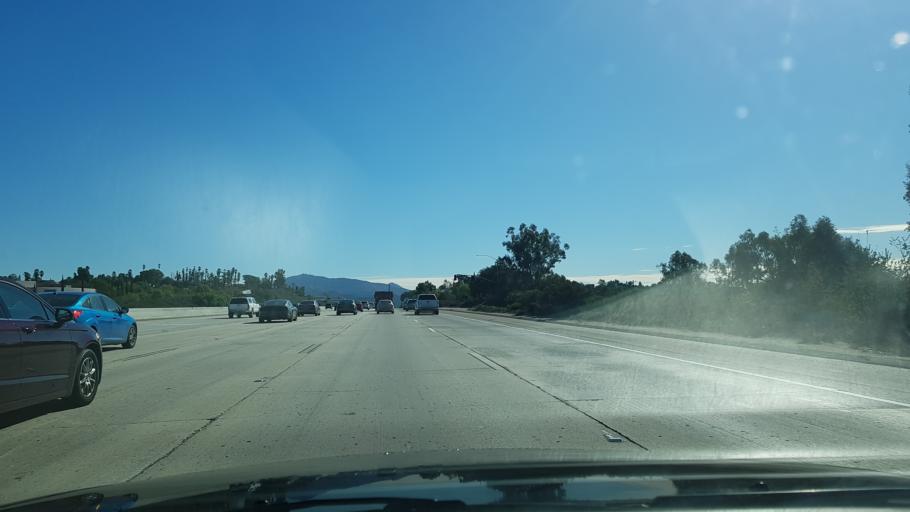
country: US
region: California
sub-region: San Diego County
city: Escondido
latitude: 33.0919
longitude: -117.0824
